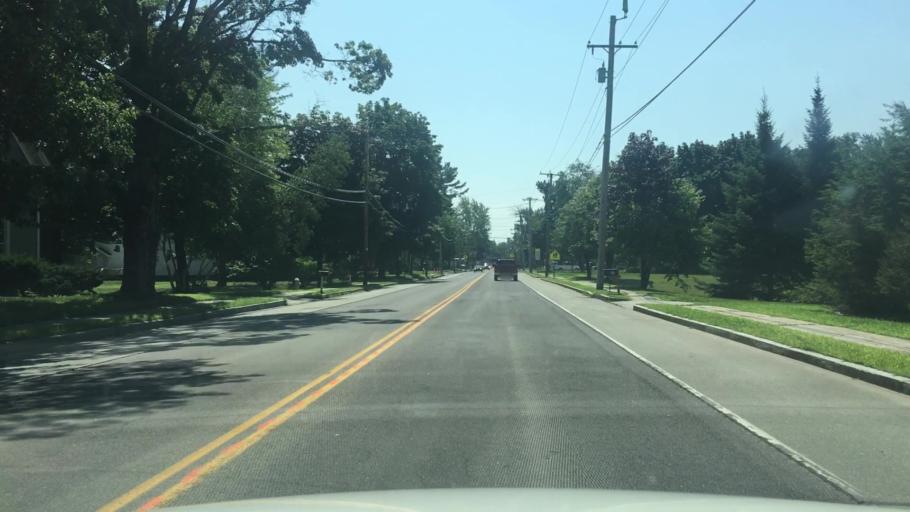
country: US
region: Maine
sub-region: Cumberland County
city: New Gloucester
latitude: 43.8897
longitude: -70.3344
